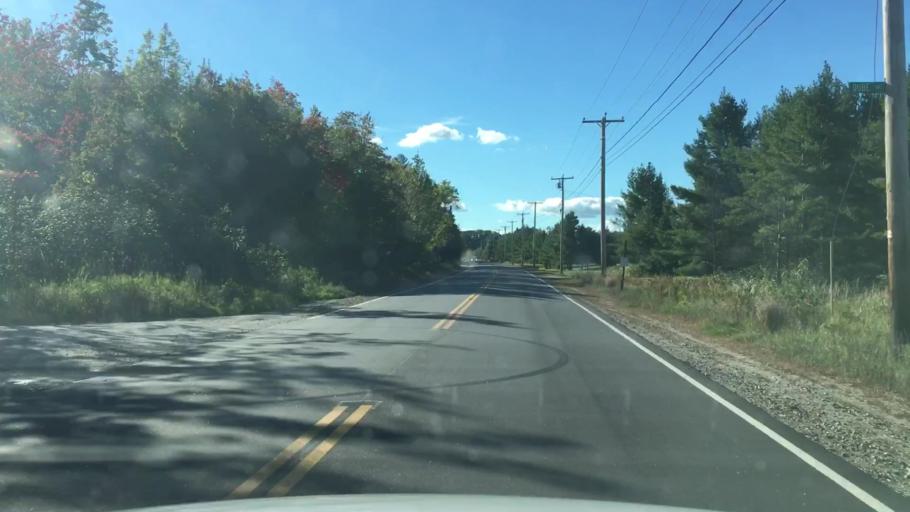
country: US
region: Maine
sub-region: Androscoggin County
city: Lisbon
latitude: 44.0721
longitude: -70.0867
